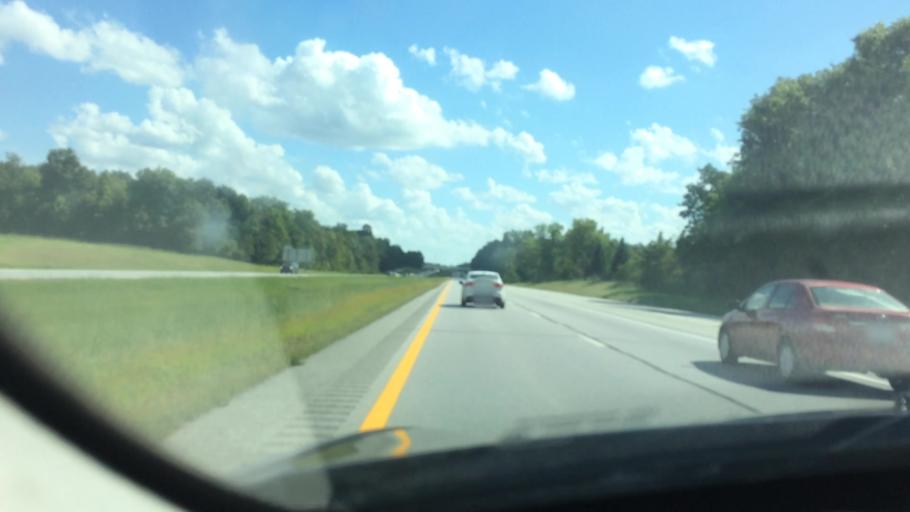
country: US
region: Ohio
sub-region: Shelby County
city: Botkins
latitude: 40.4360
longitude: -84.1694
